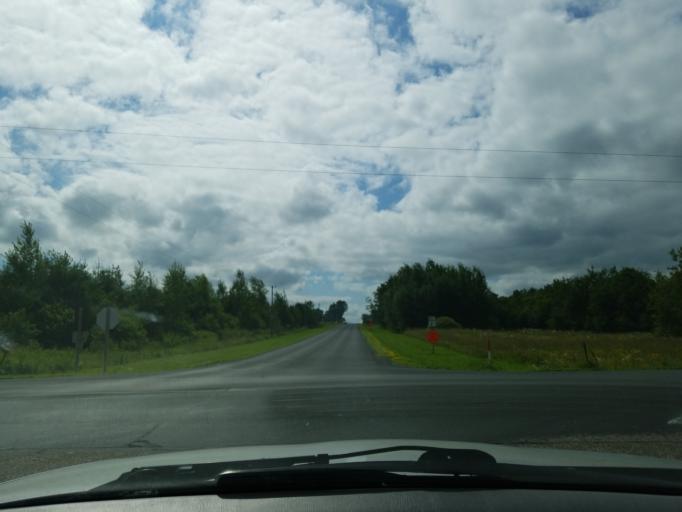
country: US
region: Wisconsin
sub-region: Saint Croix County
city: Woodville
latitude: 45.0028
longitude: -92.2575
